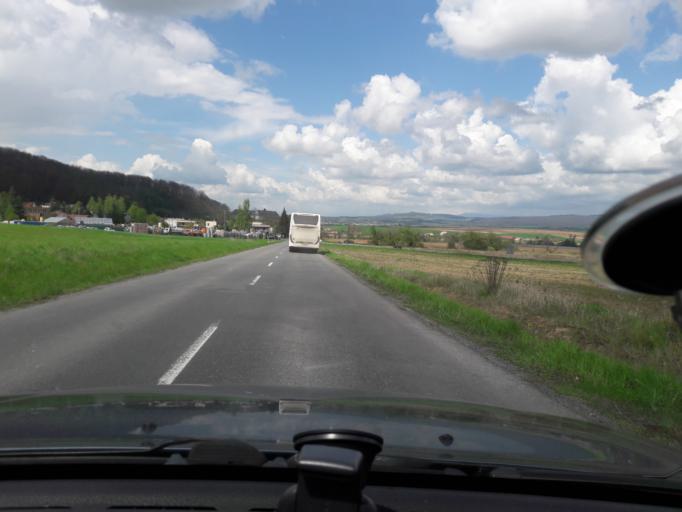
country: SK
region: Banskobystricky
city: Hrochot,Slovakia
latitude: 48.5473
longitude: 19.3043
